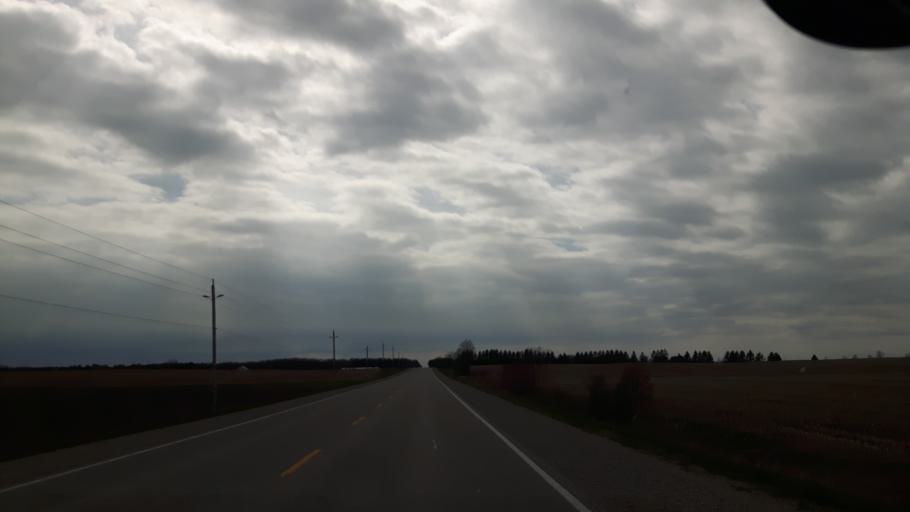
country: CA
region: Ontario
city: Bluewater
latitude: 43.5869
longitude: -81.6487
